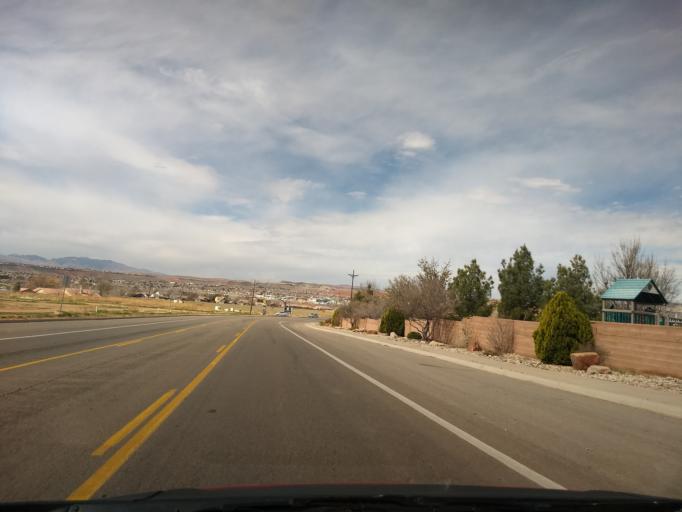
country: US
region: Utah
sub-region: Washington County
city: Washington
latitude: 37.1028
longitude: -113.4978
